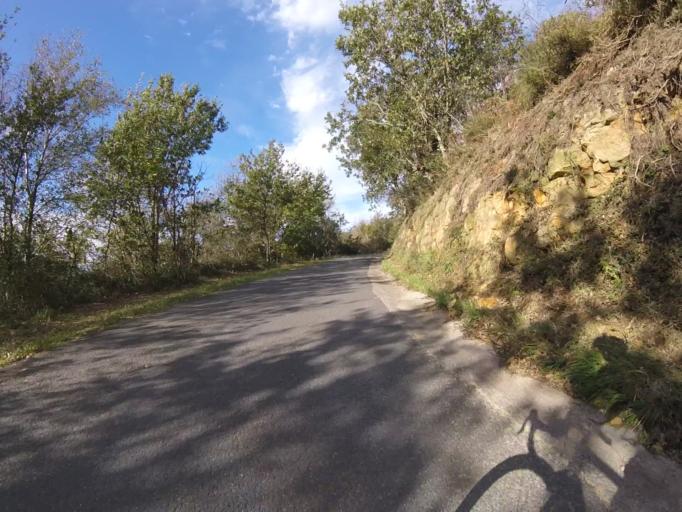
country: ES
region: Basque Country
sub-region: Provincia de Guipuzcoa
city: Orio
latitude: 43.2888
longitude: -2.0993
